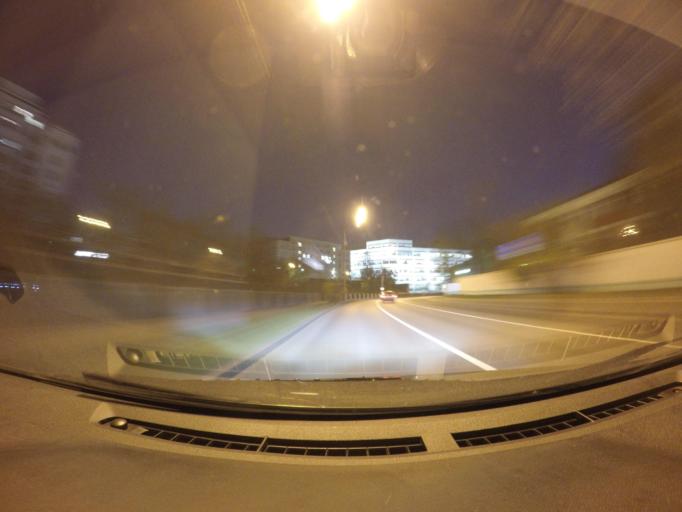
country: RU
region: Moskovskaya
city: Bogorodskoye
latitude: 55.7937
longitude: 37.7047
